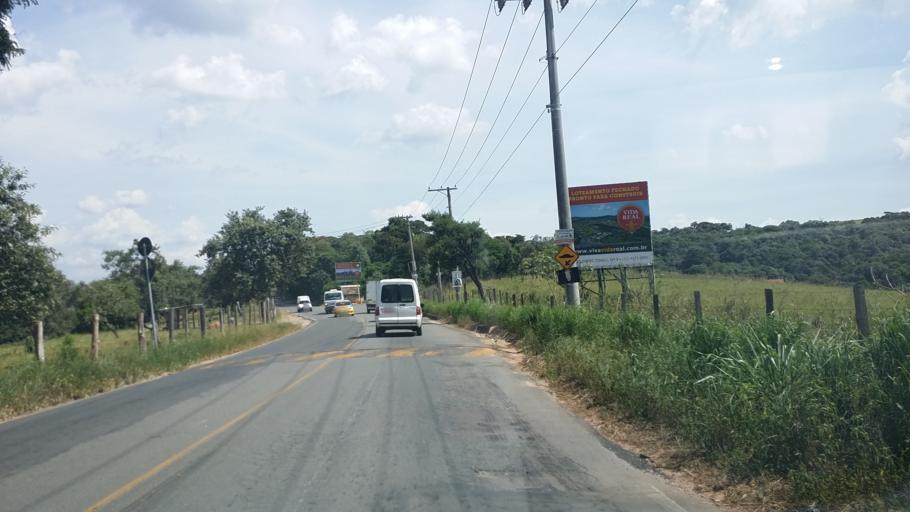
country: BR
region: Sao Paulo
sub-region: Itupeva
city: Itupeva
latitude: -23.1838
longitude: -47.0668
